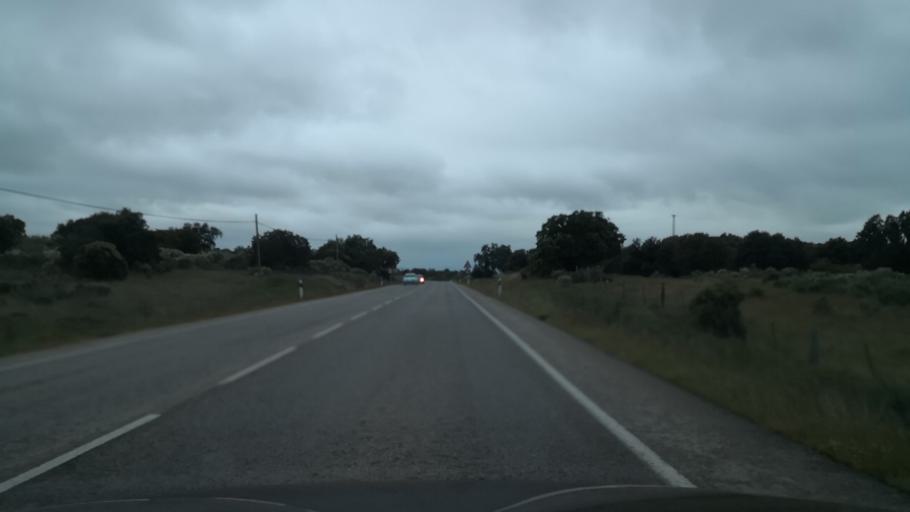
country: ES
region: Extremadura
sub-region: Provincia de Caceres
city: Caceres
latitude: 39.4027
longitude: -6.4211
